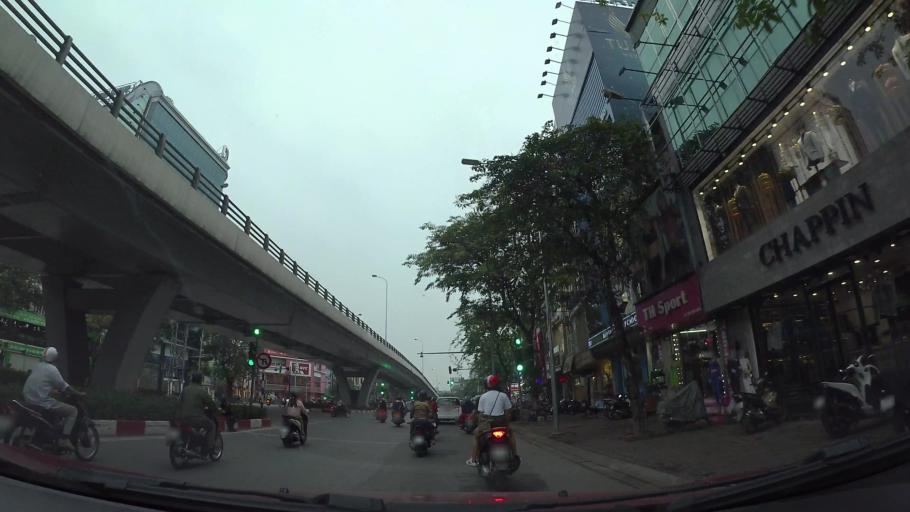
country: VN
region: Ha Noi
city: Hai BaTrung
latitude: 21.0087
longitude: 105.8507
